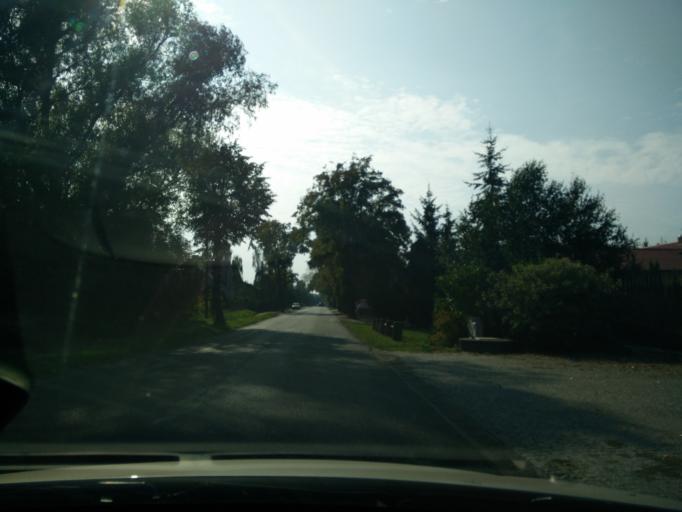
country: PL
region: Greater Poland Voivodeship
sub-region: Powiat sredzki
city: Sroda Wielkopolska
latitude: 52.2401
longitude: 17.2882
